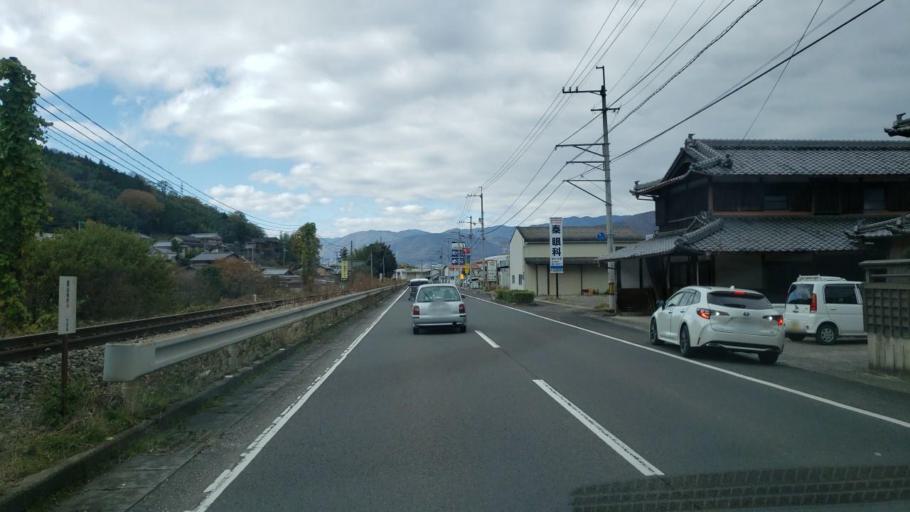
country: JP
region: Tokushima
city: Wakimachi
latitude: 34.0540
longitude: 134.1427
